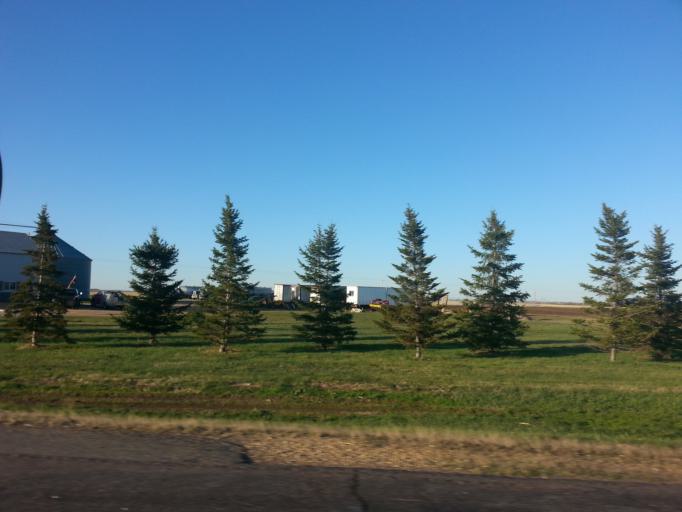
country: US
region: Wisconsin
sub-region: Pierce County
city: Prescott
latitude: 44.6863
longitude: -92.8077
